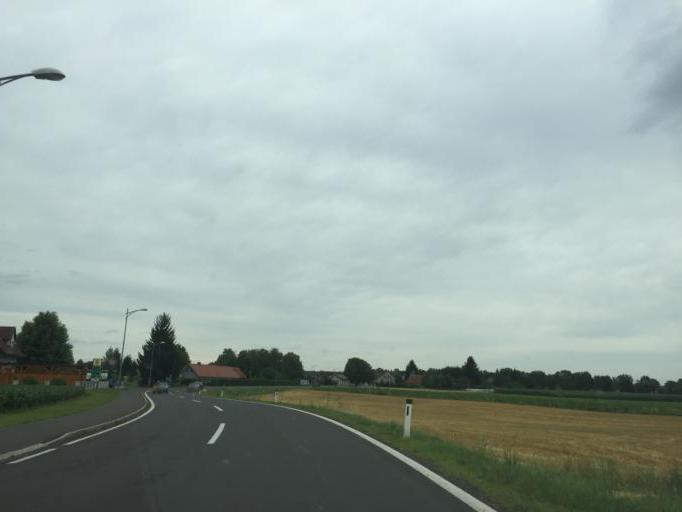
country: AT
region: Styria
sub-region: Politischer Bezirk Suedoststeiermark
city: Gosdorf
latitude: 46.7218
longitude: 15.7961
